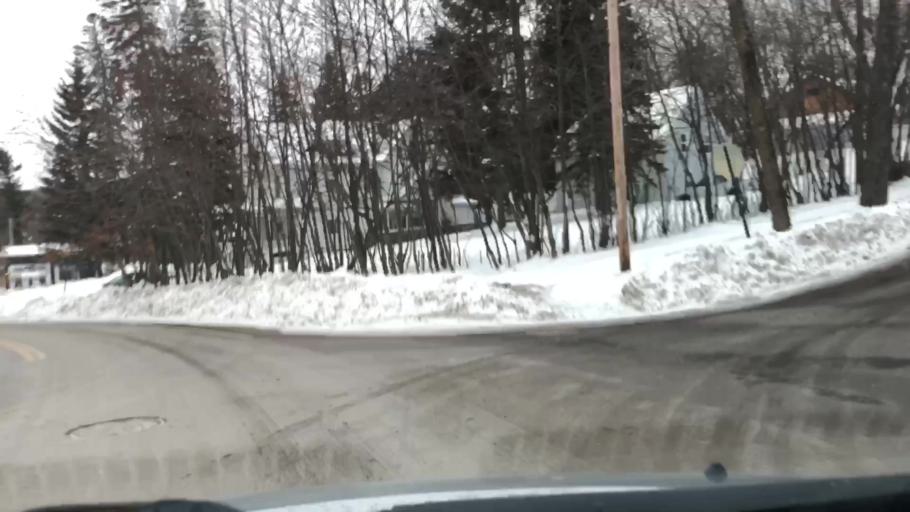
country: US
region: Minnesota
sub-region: Saint Louis County
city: Arnold
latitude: 46.8339
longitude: -92.0711
